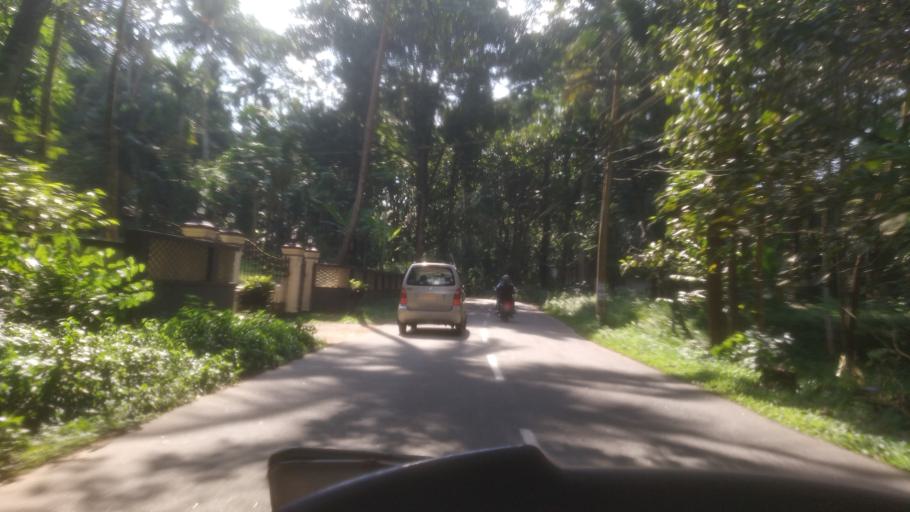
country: IN
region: Kerala
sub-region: Ernakulam
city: Kotamangalam
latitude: 10.0053
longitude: 76.7049
